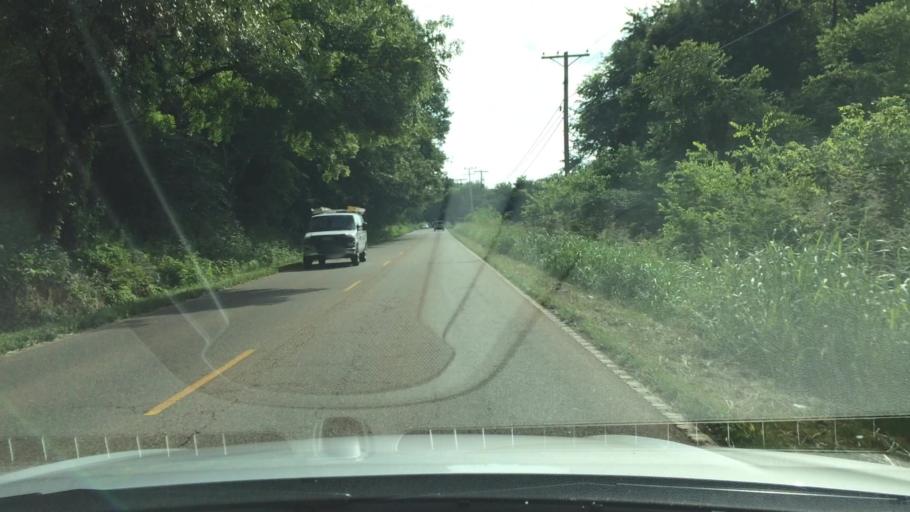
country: US
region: Tennessee
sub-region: Sevier County
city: Seymour
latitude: 35.9115
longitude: -83.6816
